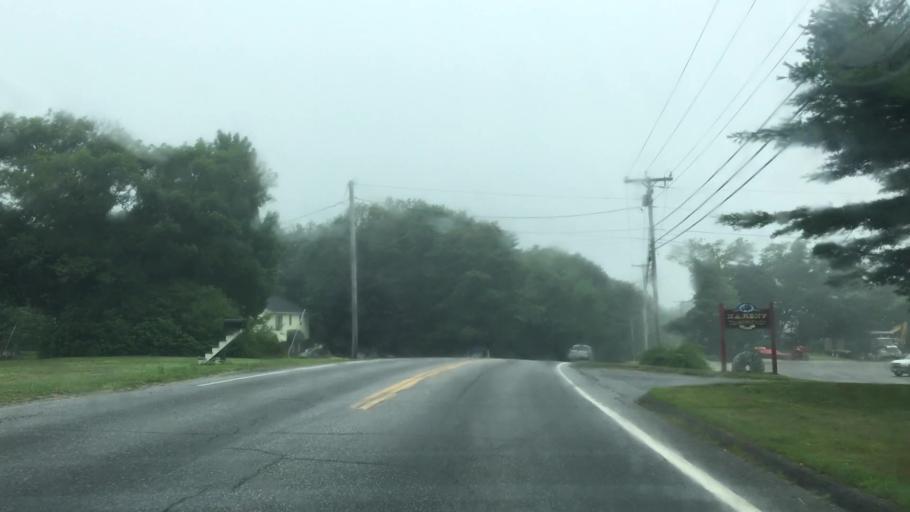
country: US
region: Maine
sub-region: Lincoln County
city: Boothbay
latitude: 43.9075
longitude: -69.6169
